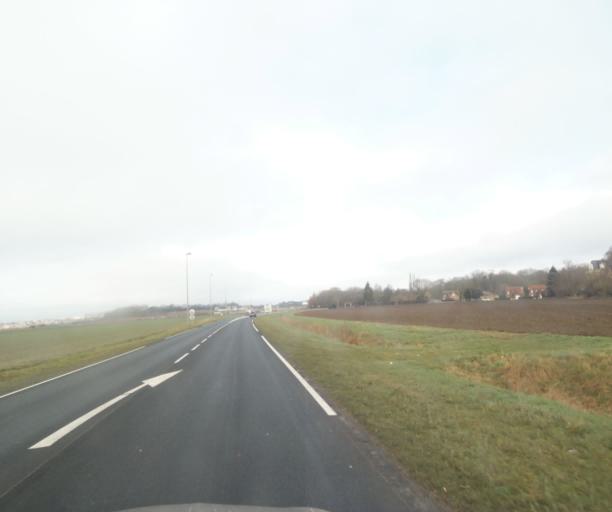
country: FR
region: Nord-Pas-de-Calais
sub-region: Departement du Nord
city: Famars
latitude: 50.3116
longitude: 3.5152
